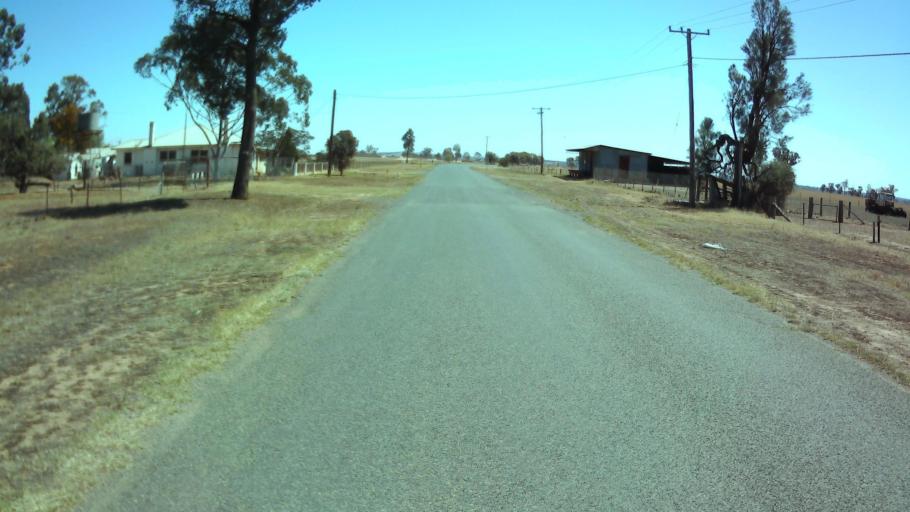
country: AU
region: New South Wales
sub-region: Weddin
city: Grenfell
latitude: -33.8413
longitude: 147.7444
